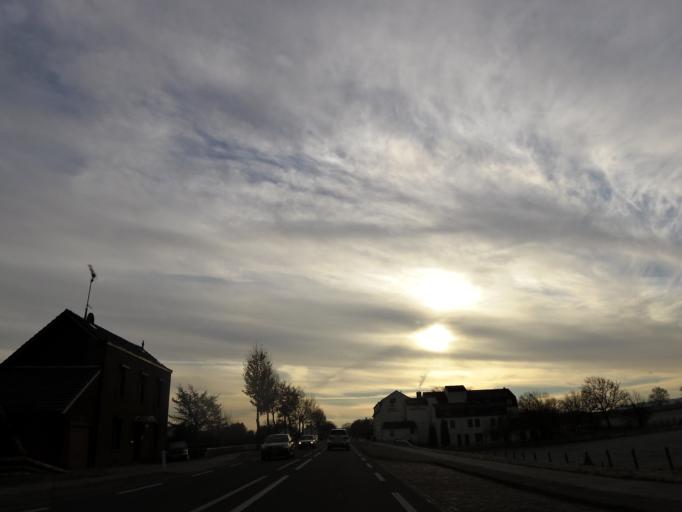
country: NL
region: Limburg
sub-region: Gemeente Simpelveld
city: Simpelveld
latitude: 50.7937
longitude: 5.9792
